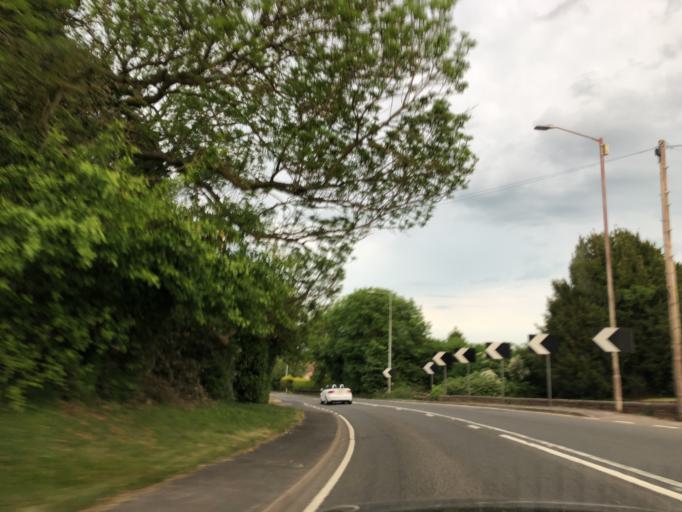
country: GB
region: England
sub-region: Warwickshire
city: Wroxall
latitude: 52.3011
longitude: -1.6477
